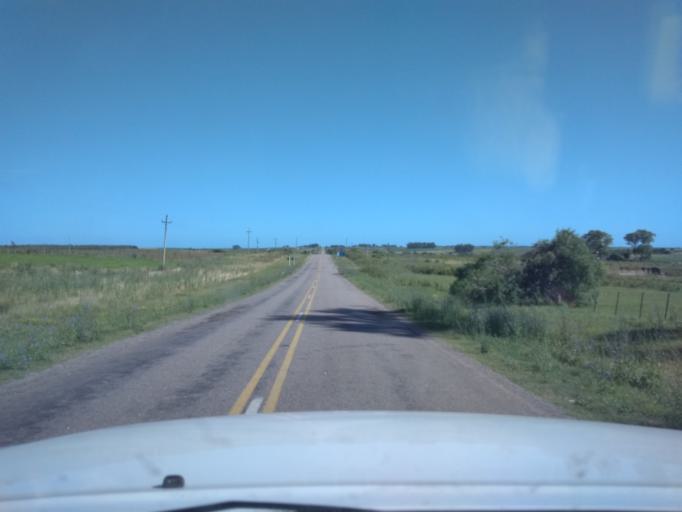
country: UY
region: Canelones
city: San Ramon
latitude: -34.1900
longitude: -55.9388
